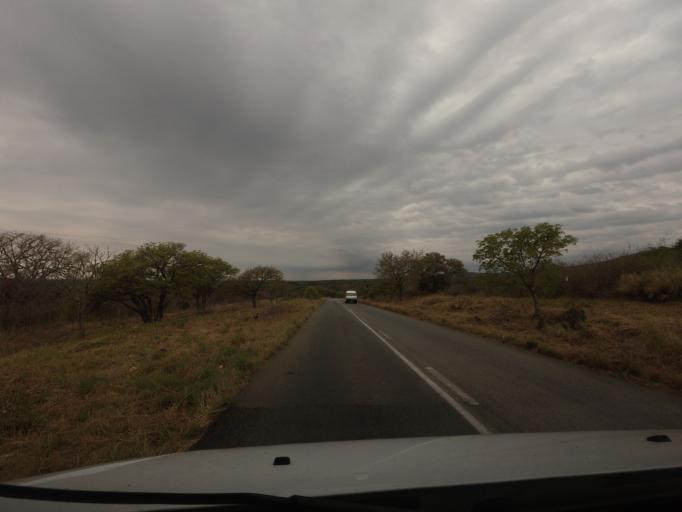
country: ZA
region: Limpopo
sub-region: Mopani District Municipality
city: Hoedspruit
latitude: -24.5075
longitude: 30.9091
